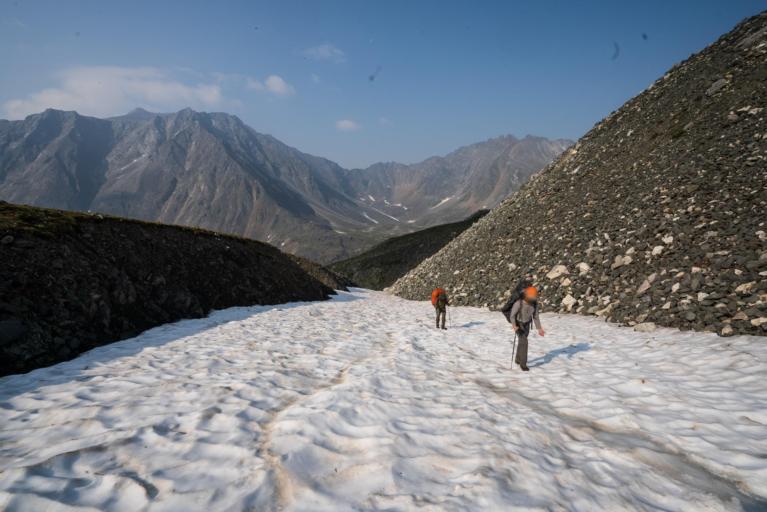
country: RU
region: Transbaikal Territory
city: Chara
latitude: 56.8254
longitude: 117.1579
